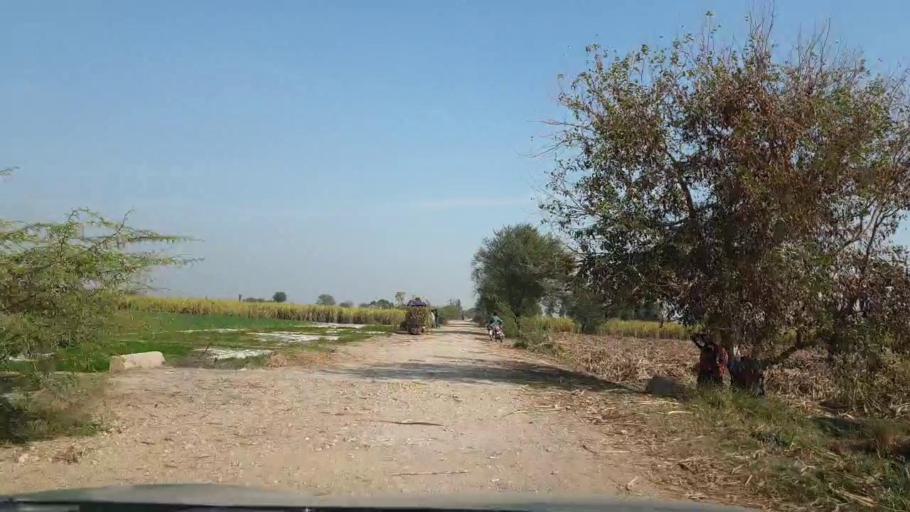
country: PK
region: Sindh
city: Berani
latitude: 25.7052
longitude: 68.7543
